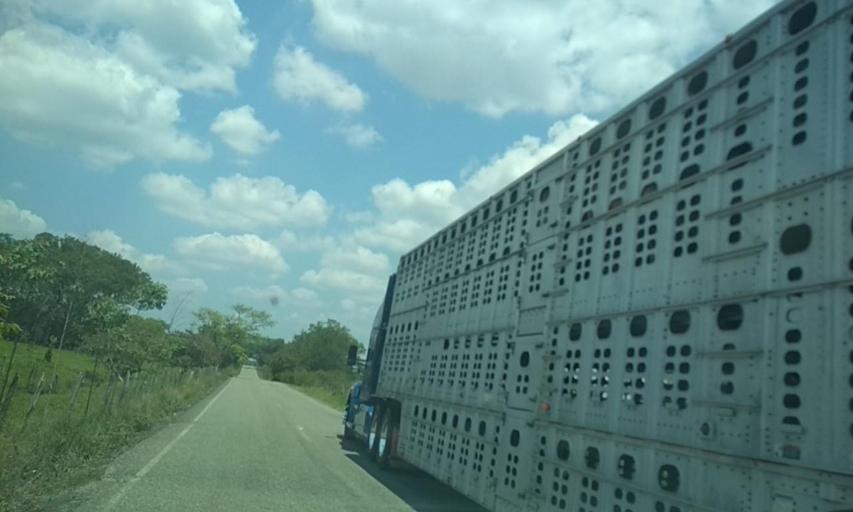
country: MX
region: Tabasco
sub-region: Huimanguillo
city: Huapacal 1ra. Seccion
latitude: 17.7563
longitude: -93.7724
